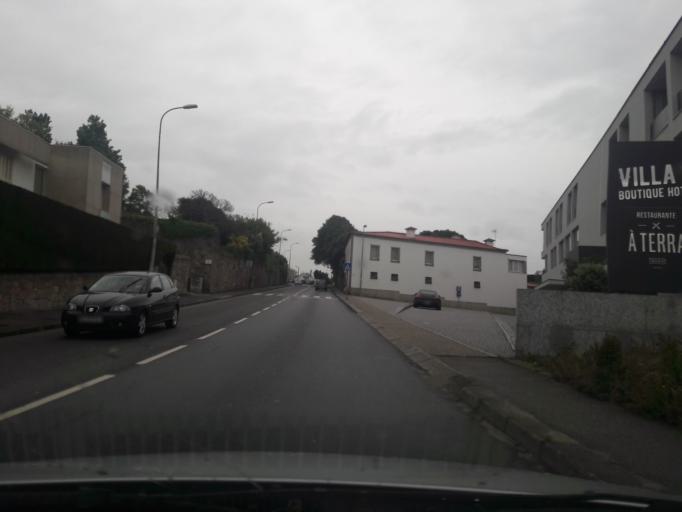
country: PT
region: Porto
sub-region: Vila do Conde
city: Vila do Conde
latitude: 41.3472
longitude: -8.7383
